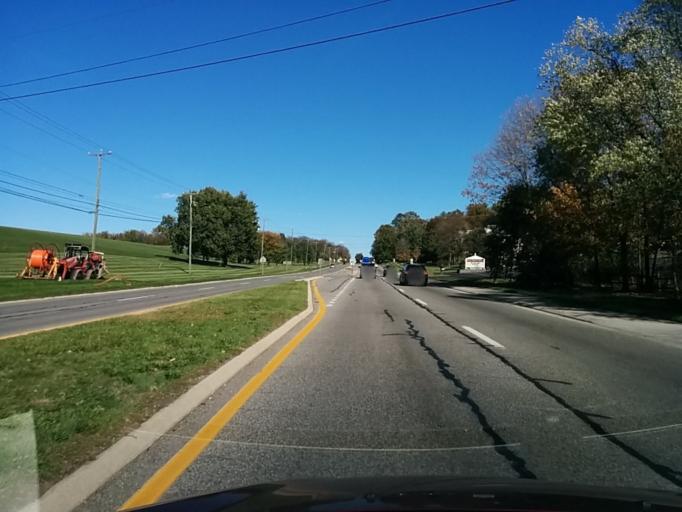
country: US
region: Virginia
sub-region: Roanoke County
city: Hollins
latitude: 37.3518
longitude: -79.9401
